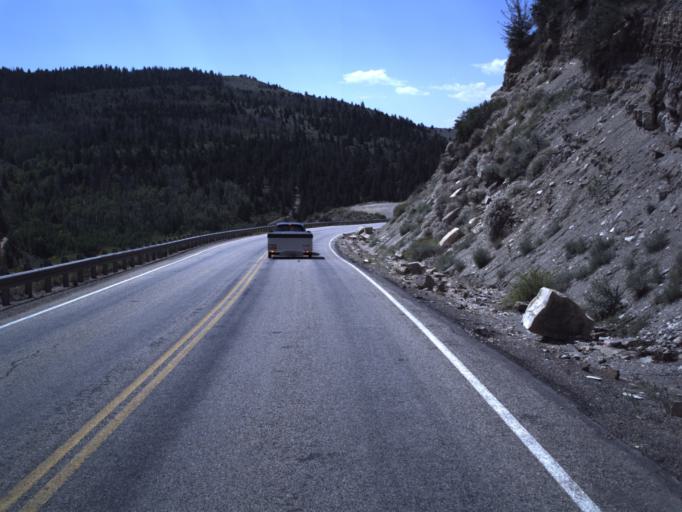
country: US
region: Utah
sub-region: Carbon County
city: Helper
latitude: 39.8492
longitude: -110.7663
